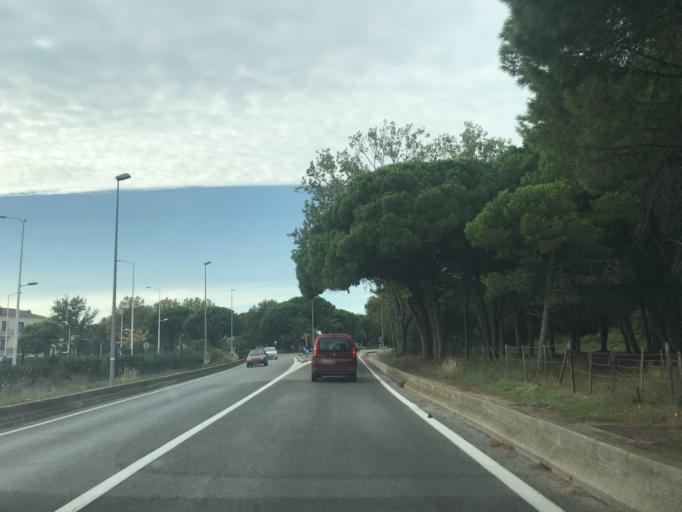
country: FR
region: Languedoc-Roussillon
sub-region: Departement du Gard
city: Le Grau-du-Roi
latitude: 43.5506
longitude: 4.1196
